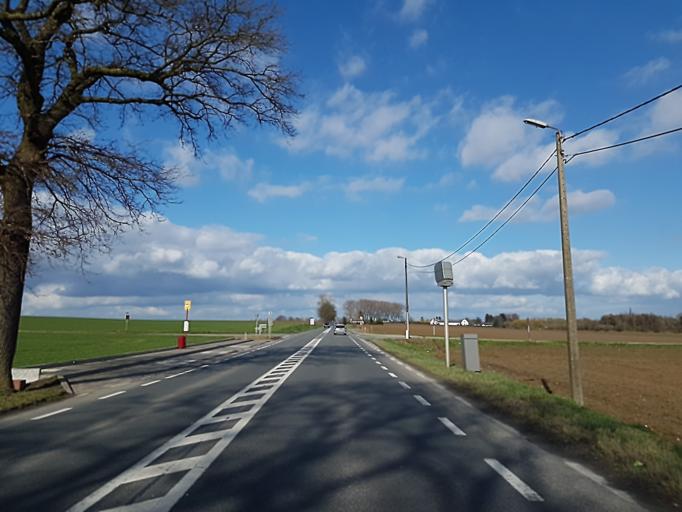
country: BE
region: Wallonia
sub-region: Province du Brabant Wallon
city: Perwez
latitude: 50.6548
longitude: 4.8036
